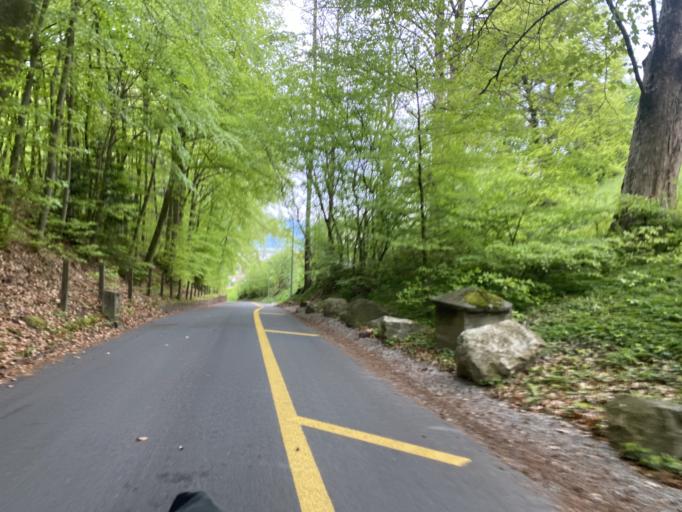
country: CH
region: Bern
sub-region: Thun District
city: Thun
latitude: 46.7489
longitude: 7.6425
